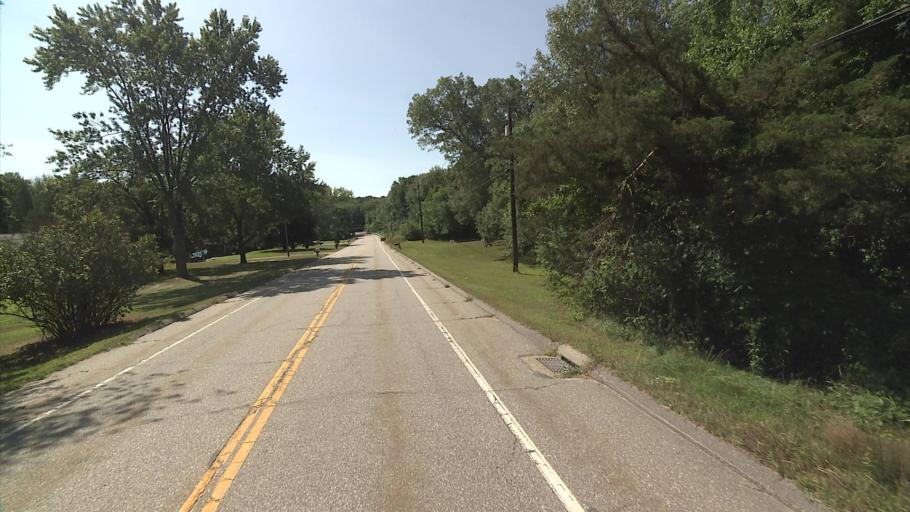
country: US
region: Connecticut
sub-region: New London County
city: Baltic
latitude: 41.6229
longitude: -72.1183
